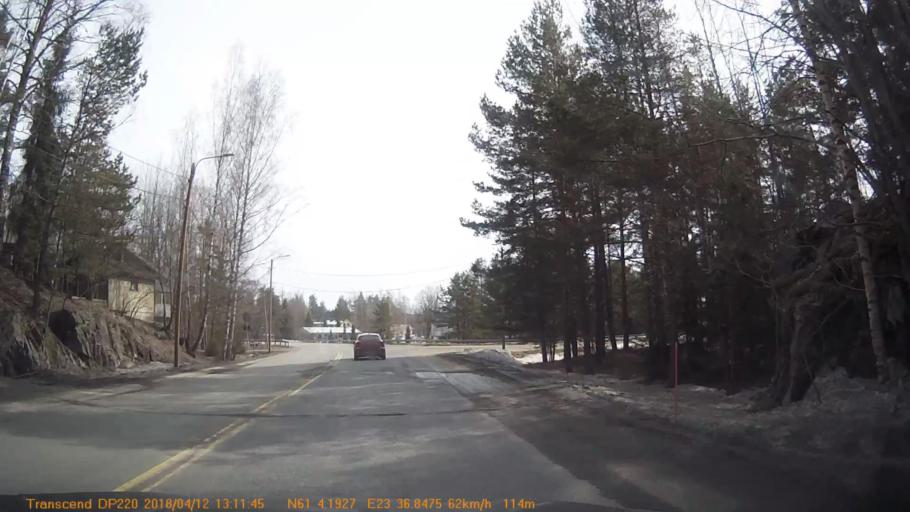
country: FI
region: Pirkanmaa
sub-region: Etelae-Pirkanmaa
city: Urjala
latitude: 61.0695
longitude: 23.6152
